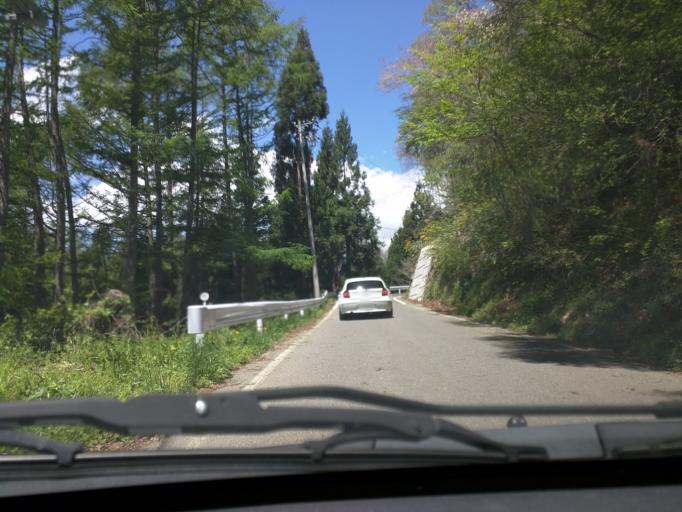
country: JP
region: Nagano
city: Nagano-shi
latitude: 36.6909
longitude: 138.1079
